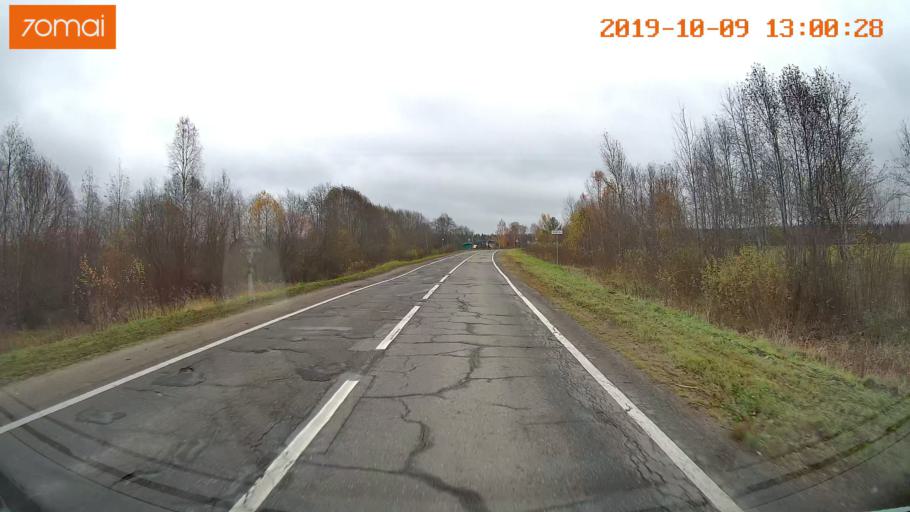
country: RU
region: Jaroslavl
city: Prechistoye
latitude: 58.3770
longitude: 40.4806
